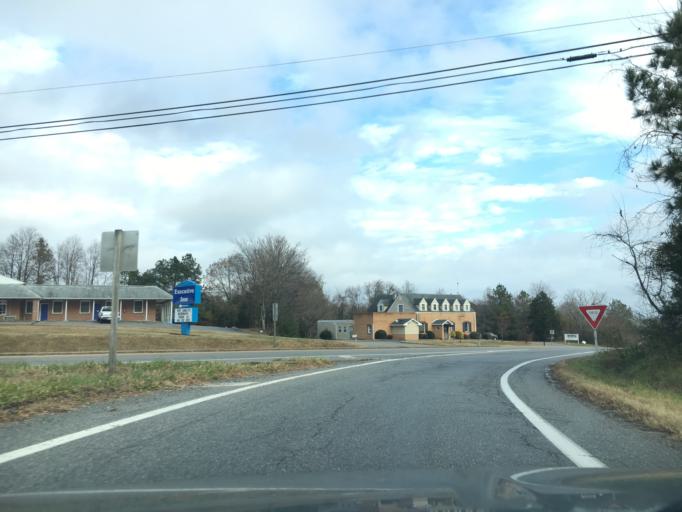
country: US
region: Virginia
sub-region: Prince Edward County
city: Farmville
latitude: 37.3162
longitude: -78.4599
